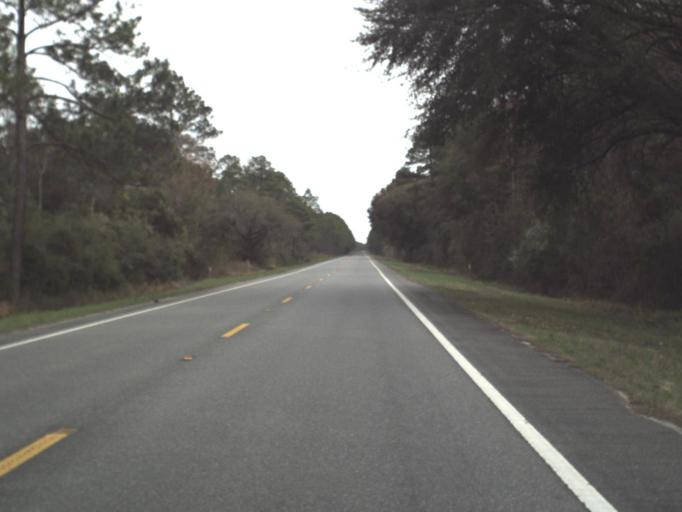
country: US
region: Florida
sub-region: Gadsden County
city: Midway
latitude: 30.3371
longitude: -84.4839
